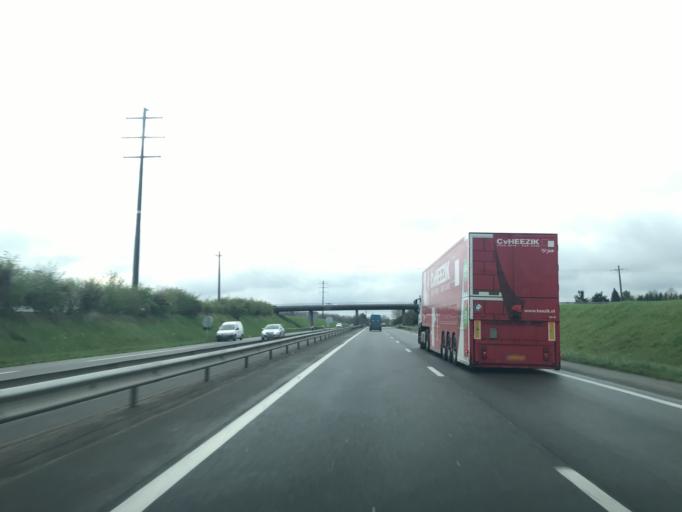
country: FR
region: Centre
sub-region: Departement du Loiret
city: Boigny-sur-Bionne
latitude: 47.9147
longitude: 2.0158
